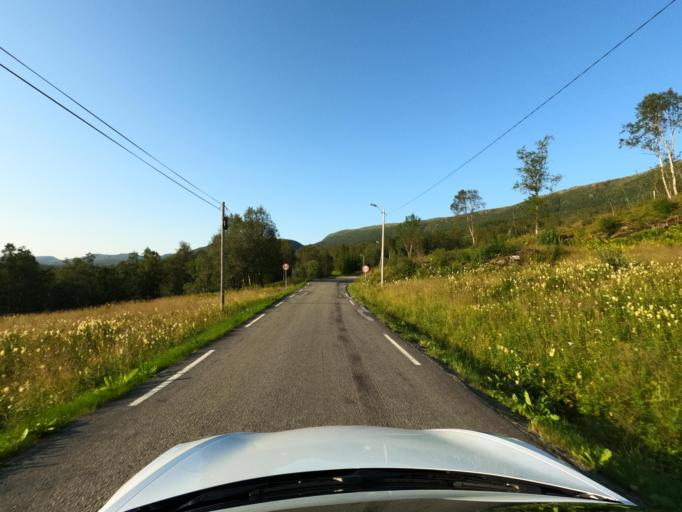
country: NO
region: Nordland
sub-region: Ballangen
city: Ballangen
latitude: 68.5234
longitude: 16.7635
